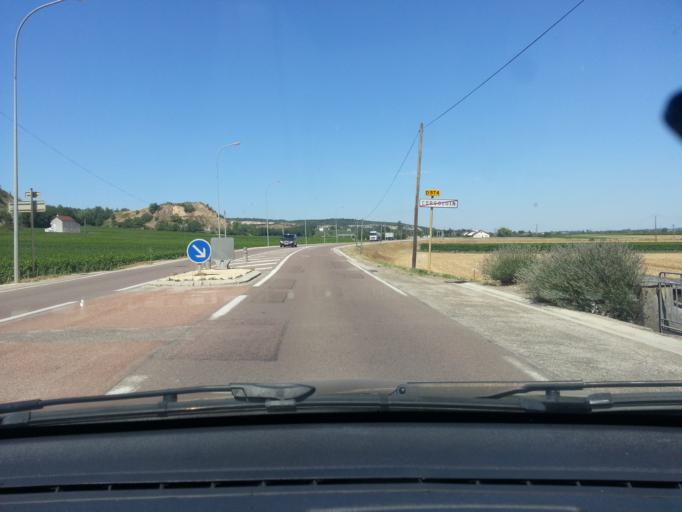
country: FR
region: Bourgogne
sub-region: Departement de la Cote-d'Or
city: Nuits-Saint-Georges
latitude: 47.0887
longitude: 4.9061
